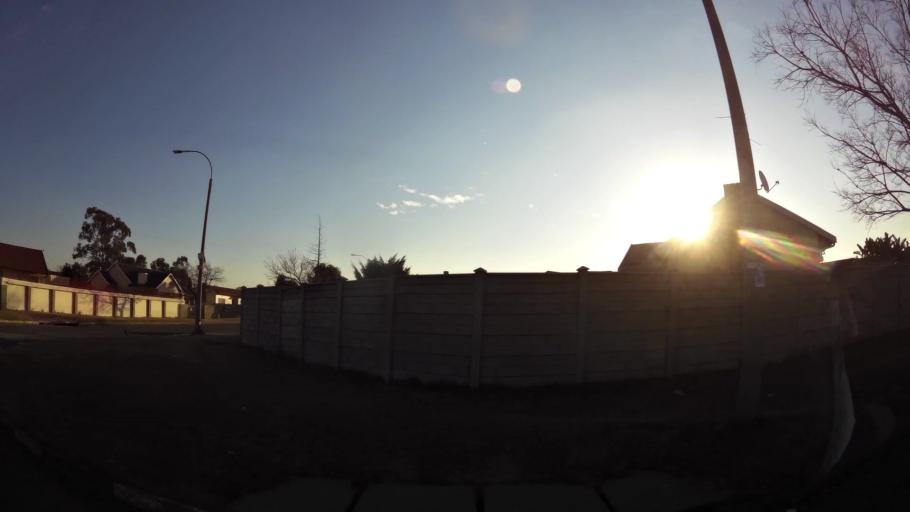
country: ZA
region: Gauteng
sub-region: West Rand District Municipality
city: Randfontein
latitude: -26.2081
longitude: 27.6519
